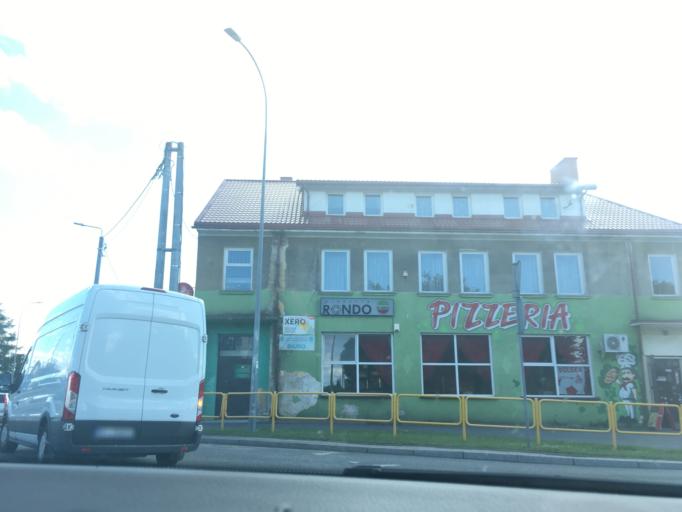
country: PL
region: Podlasie
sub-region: Powiat bialostocki
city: Zabludow
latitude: 53.0143
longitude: 23.3382
